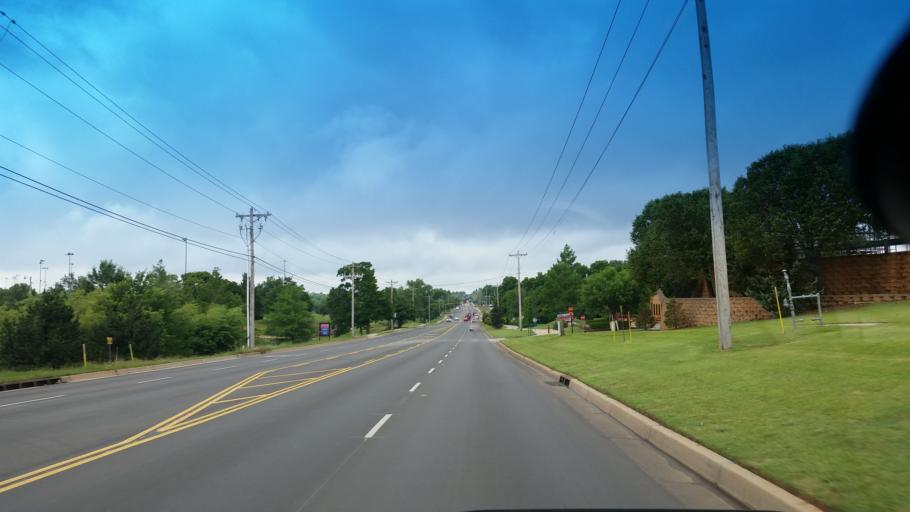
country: US
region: Oklahoma
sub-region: Oklahoma County
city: Edmond
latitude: 35.6494
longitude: -97.4605
